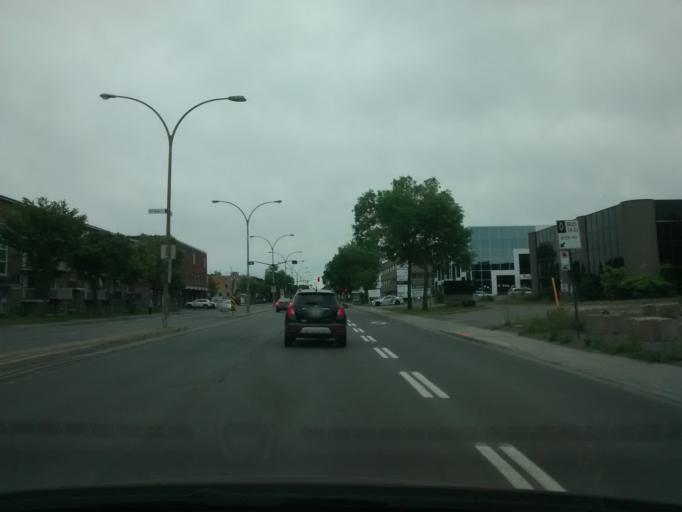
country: CA
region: Quebec
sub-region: Montreal
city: Saint-Leonard
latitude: 45.5785
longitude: -73.6186
